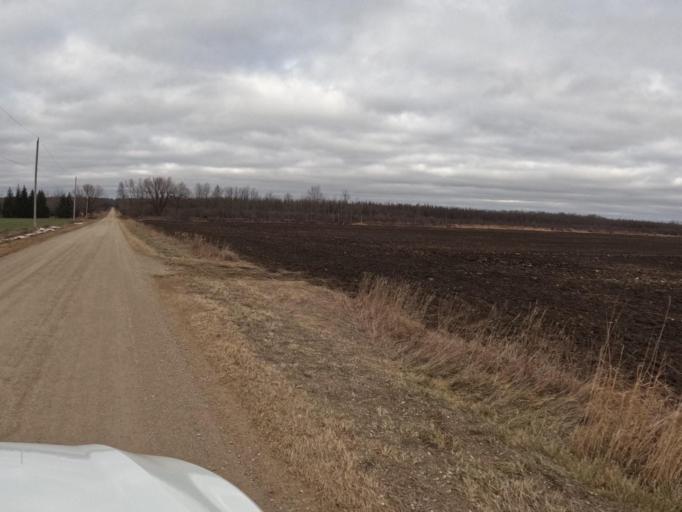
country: CA
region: Ontario
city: Shelburne
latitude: 43.8937
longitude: -80.4071
